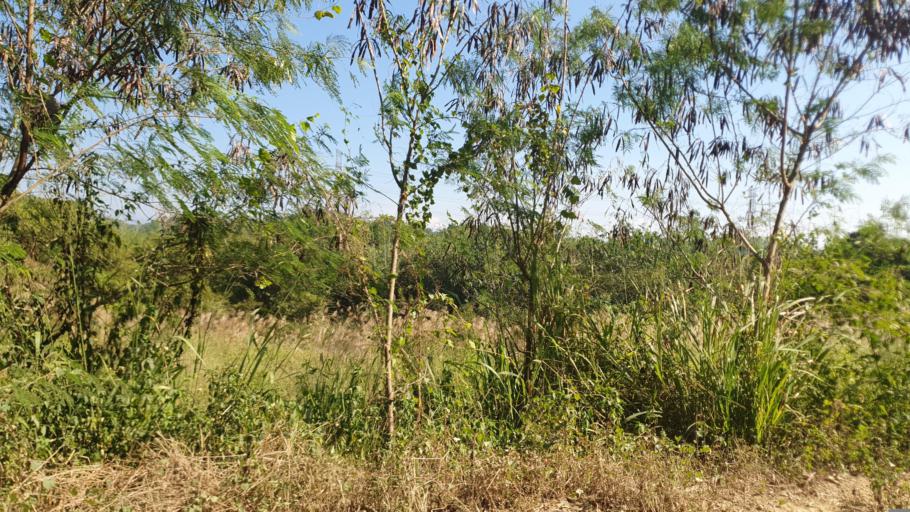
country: TW
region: Taiwan
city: Yujing
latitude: 23.0491
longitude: 120.3726
